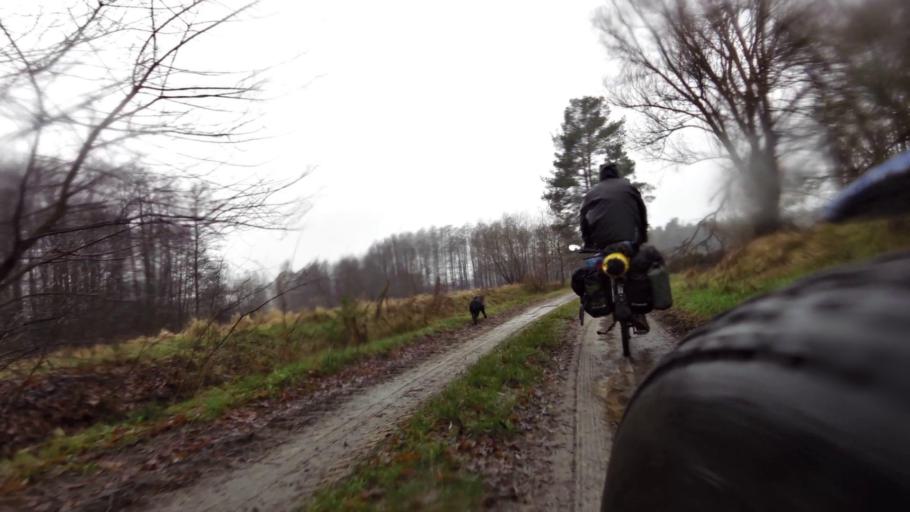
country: PL
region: West Pomeranian Voivodeship
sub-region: Powiat drawski
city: Zlocieniec
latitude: 53.5487
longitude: 15.9406
